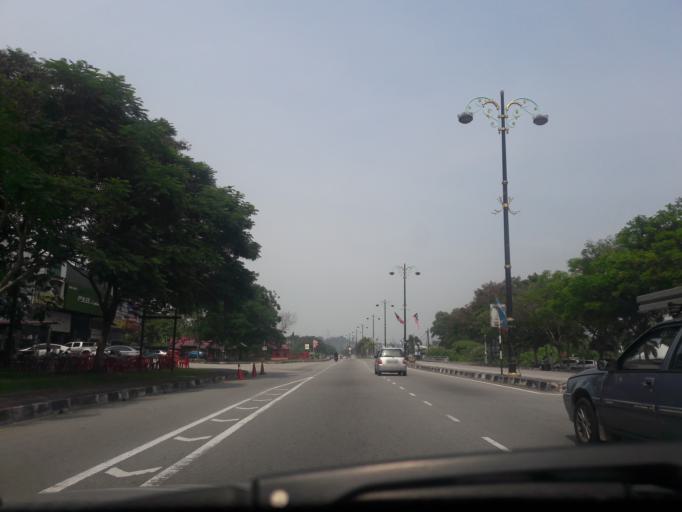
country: MY
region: Kedah
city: Kulim
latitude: 5.3877
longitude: 100.5612
